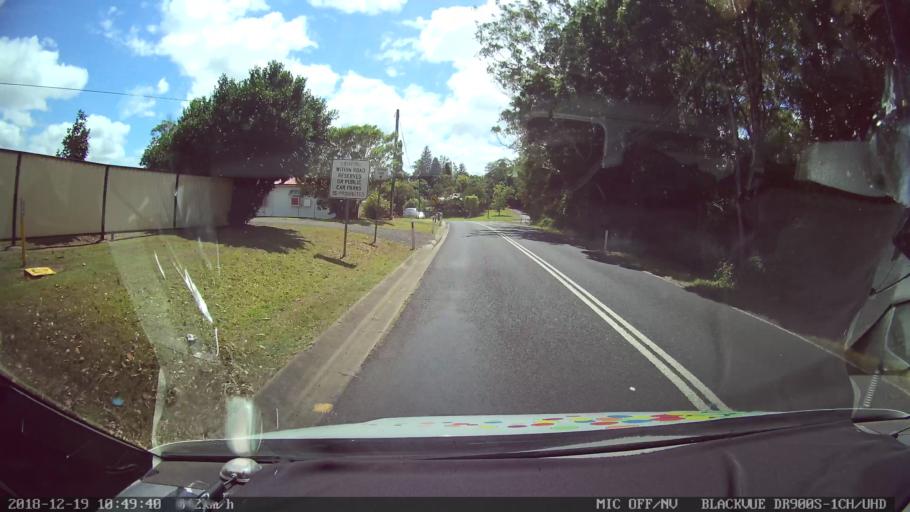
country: AU
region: New South Wales
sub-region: Lismore Municipality
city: Nimbin
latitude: -28.6012
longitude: 153.2204
